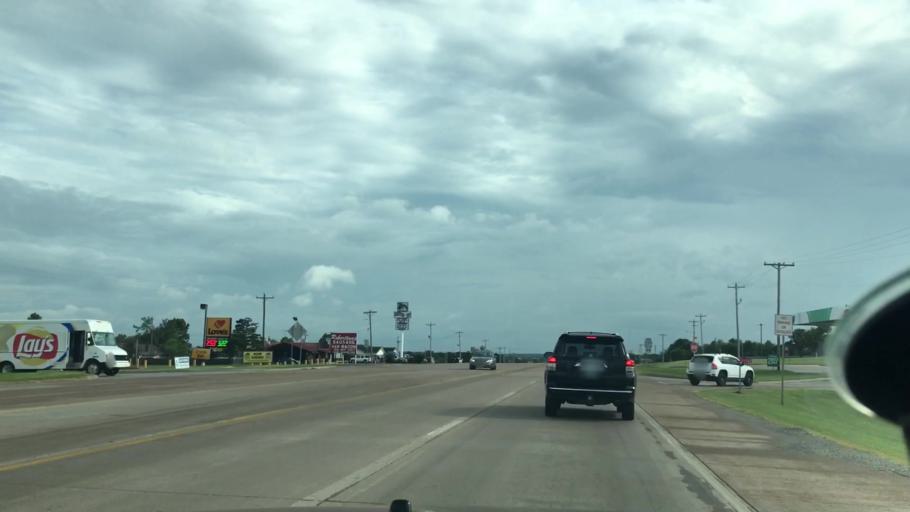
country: US
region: Oklahoma
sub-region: Lincoln County
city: Prague
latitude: 35.3823
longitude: -96.6715
